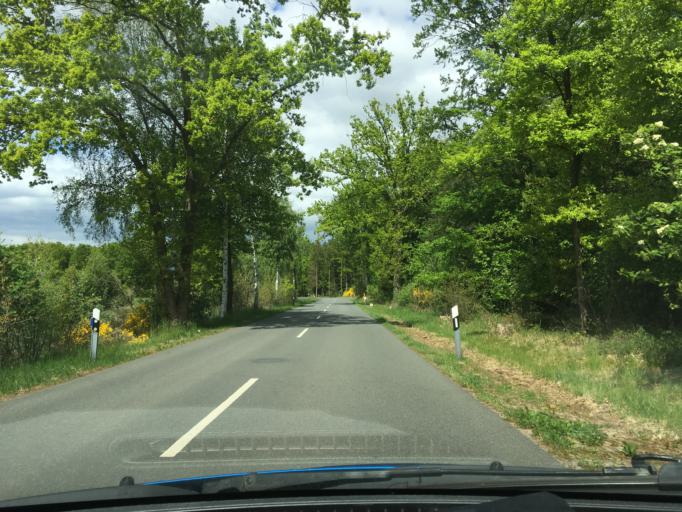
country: DE
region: Lower Saxony
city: Suderburg
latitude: 52.9156
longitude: 10.4695
